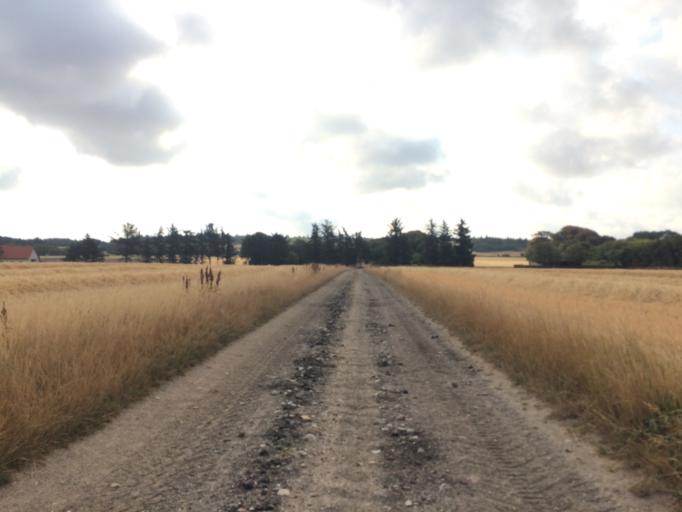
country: DK
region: Central Jutland
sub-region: Holstebro Kommune
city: Vinderup
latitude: 56.6152
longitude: 8.7294
